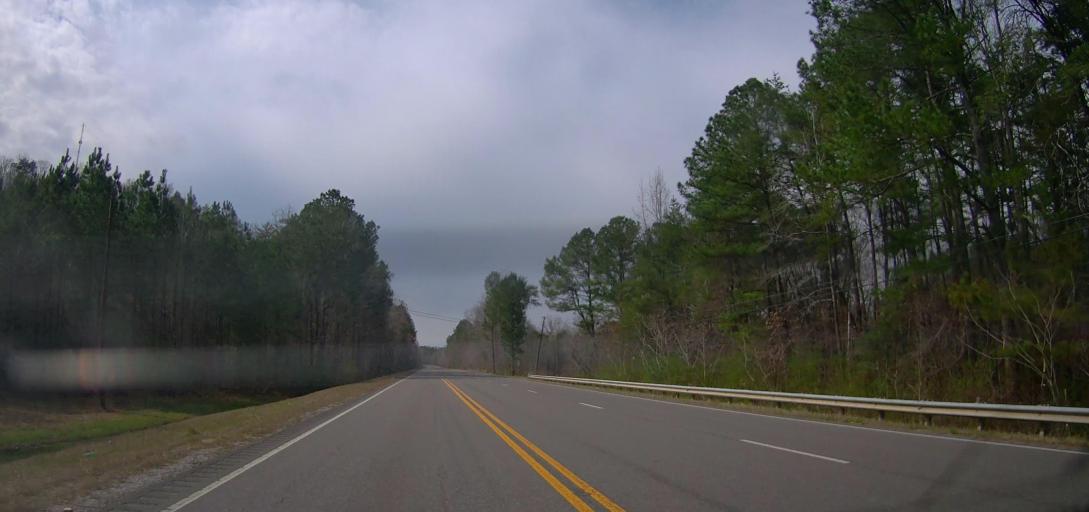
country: US
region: Alabama
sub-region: Walker County
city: Carbon Hill
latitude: 33.9101
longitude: -87.5582
